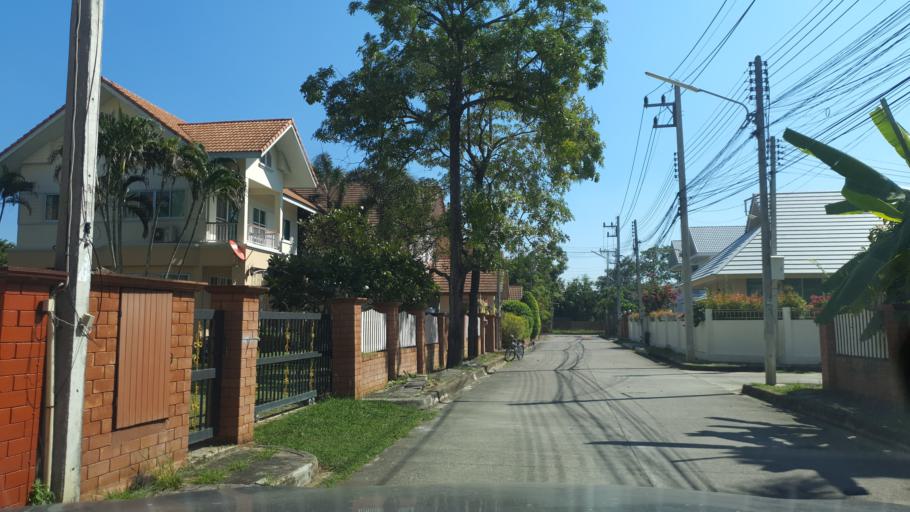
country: TH
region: Chiang Mai
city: Hang Dong
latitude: 18.7319
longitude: 98.9448
